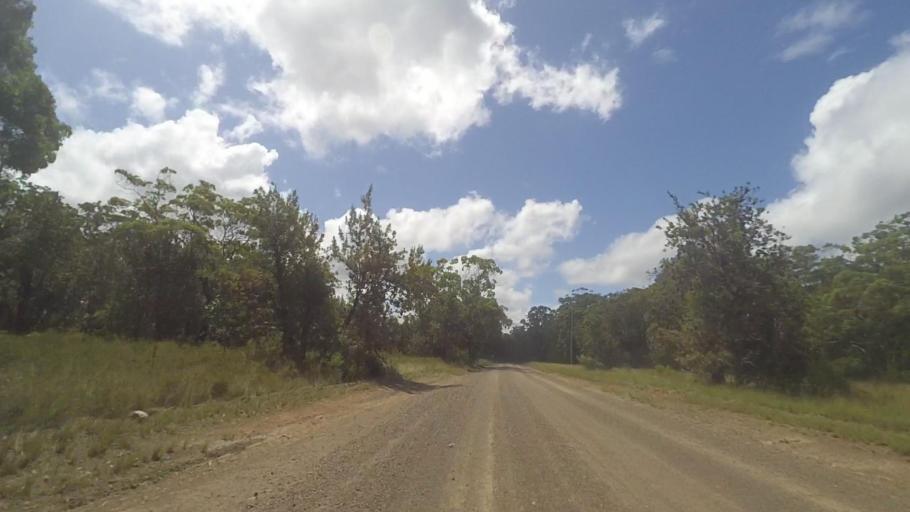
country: AU
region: New South Wales
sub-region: Great Lakes
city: Bulahdelah
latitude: -32.5051
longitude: 152.2913
